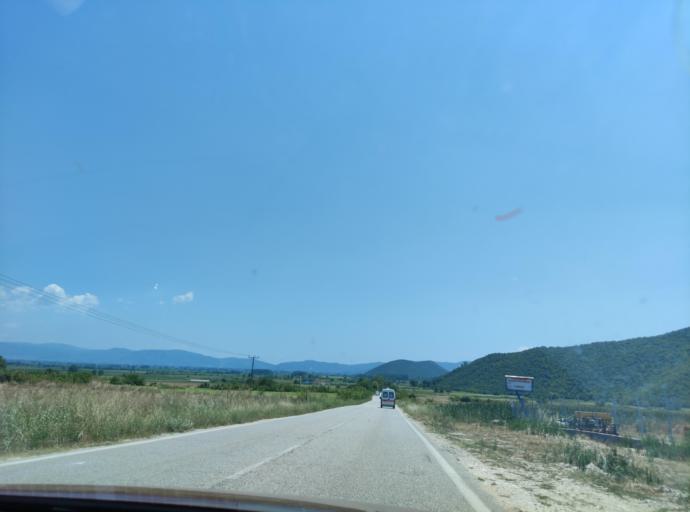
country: GR
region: East Macedonia and Thrace
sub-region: Nomos Kavalas
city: Palaiochori
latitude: 40.9711
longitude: 24.1658
